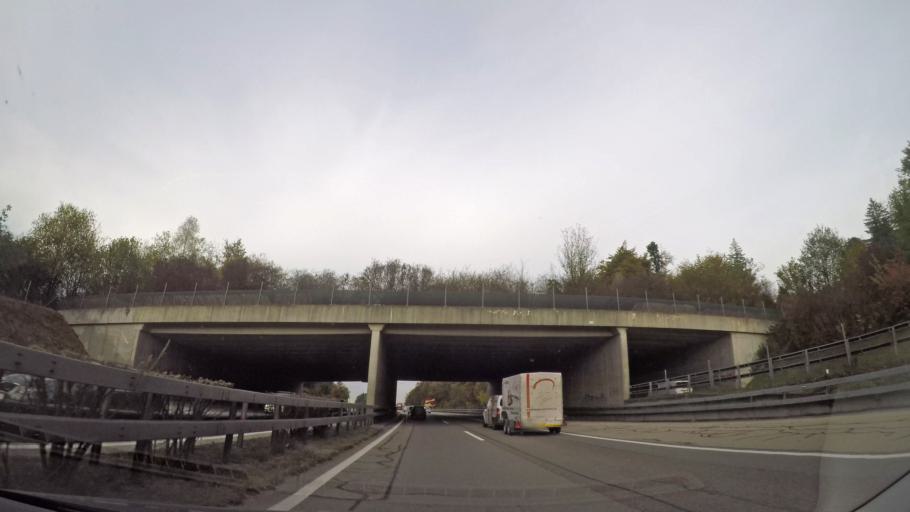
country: CH
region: Bern
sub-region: Emmental District
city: Lyssach
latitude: 47.0619
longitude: 7.5578
